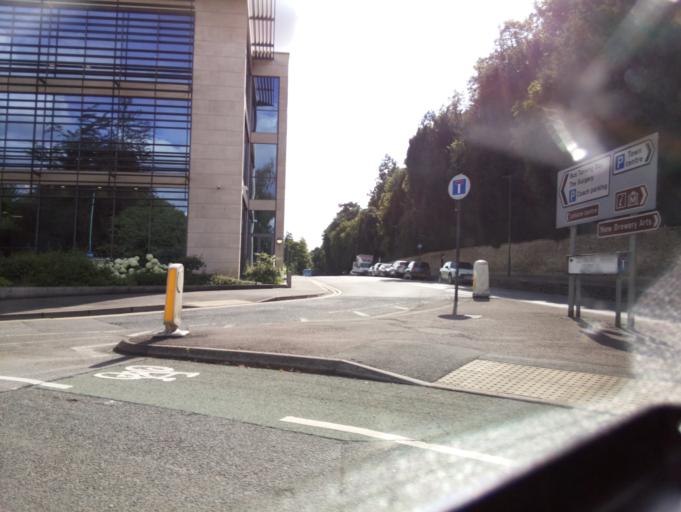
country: GB
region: England
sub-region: Gloucestershire
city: Cirencester
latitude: 51.7151
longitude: -1.9732
